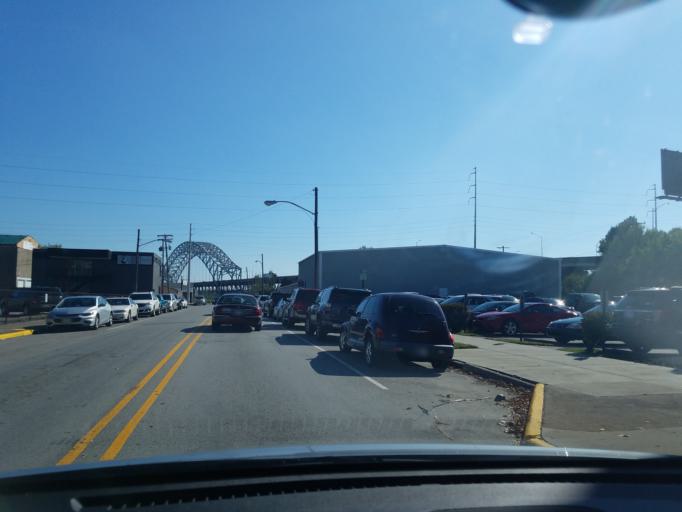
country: US
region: Indiana
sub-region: Floyd County
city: New Albany
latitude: 38.2838
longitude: -85.8256
